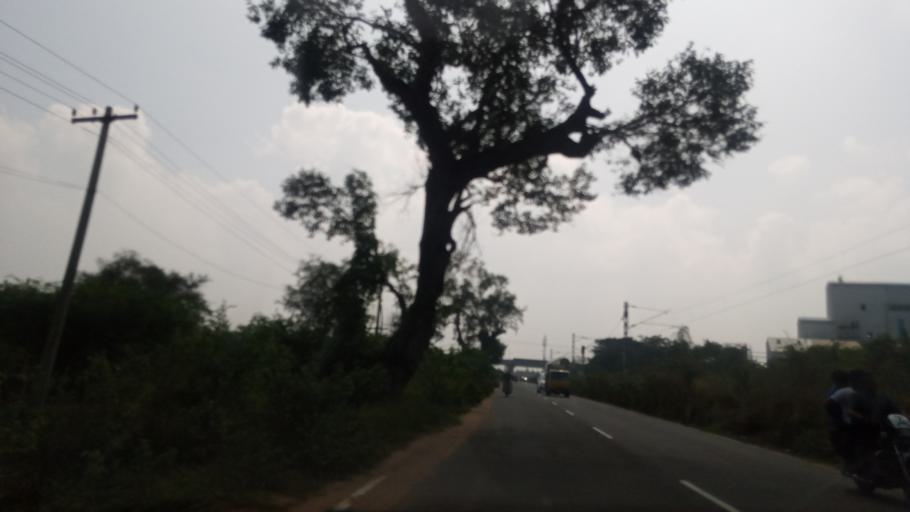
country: IN
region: Tamil Nadu
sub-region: Kancheepuram
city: Kanchipuram
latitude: 12.8778
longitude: 79.6898
